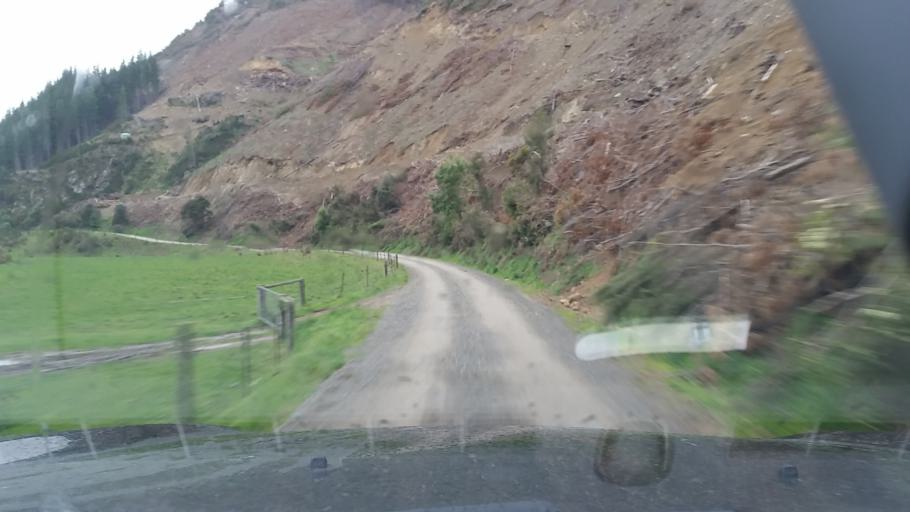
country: NZ
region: Marlborough
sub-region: Marlborough District
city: Blenheim
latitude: -41.4020
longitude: 173.8483
